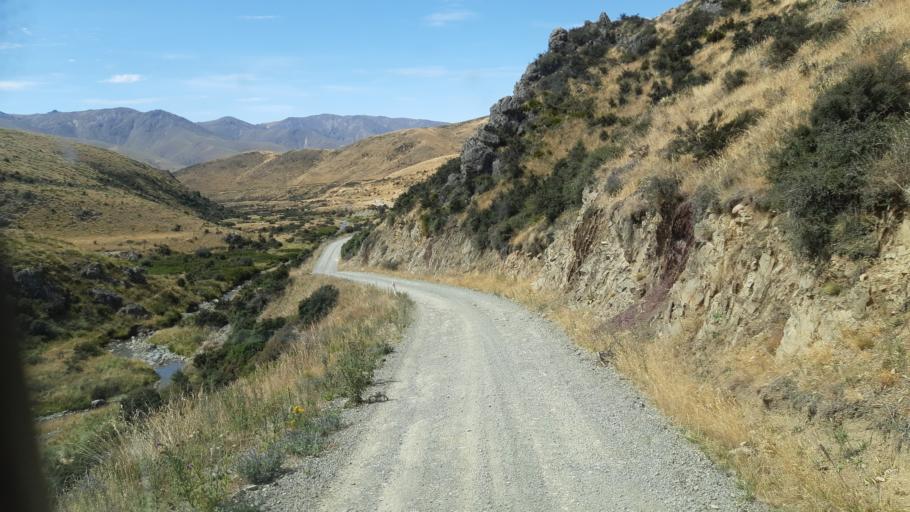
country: NZ
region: Canterbury
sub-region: Timaru District
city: Pleasant Point
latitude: -44.3508
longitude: 170.6015
